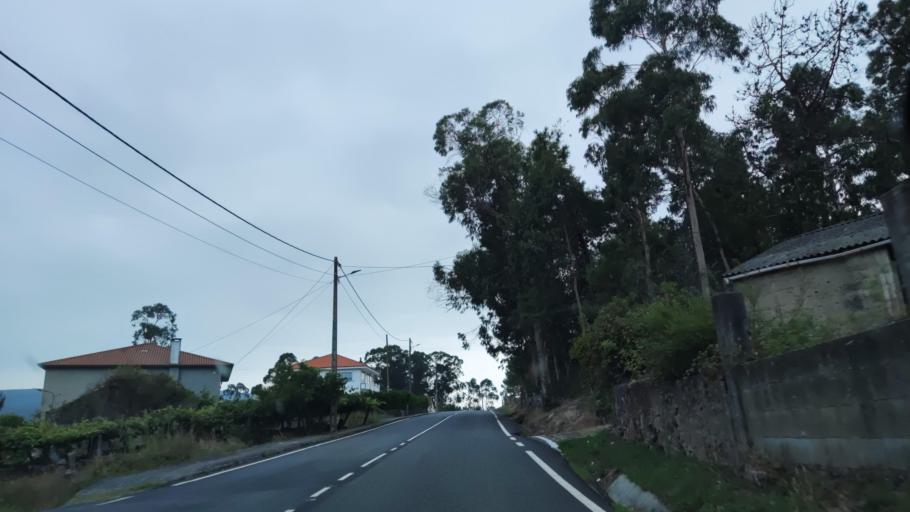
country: ES
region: Galicia
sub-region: Provincia de Pontevedra
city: Catoira
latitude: 42.6652
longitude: -8.7447
